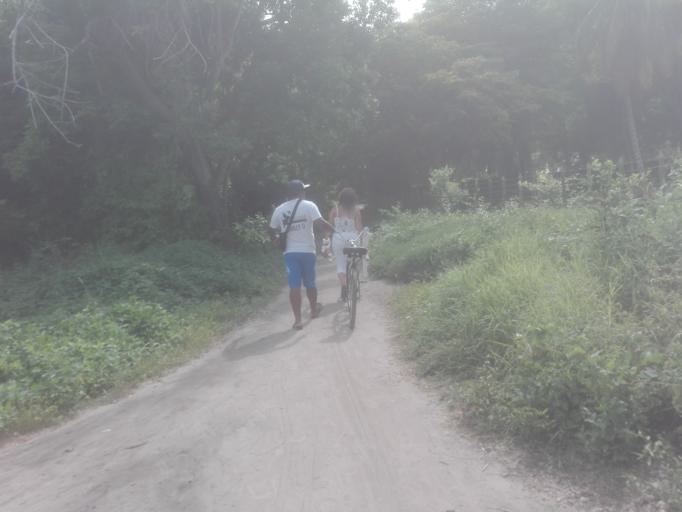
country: CO
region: Bolivar
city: Turbana
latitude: 10.1798
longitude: -75.7369
